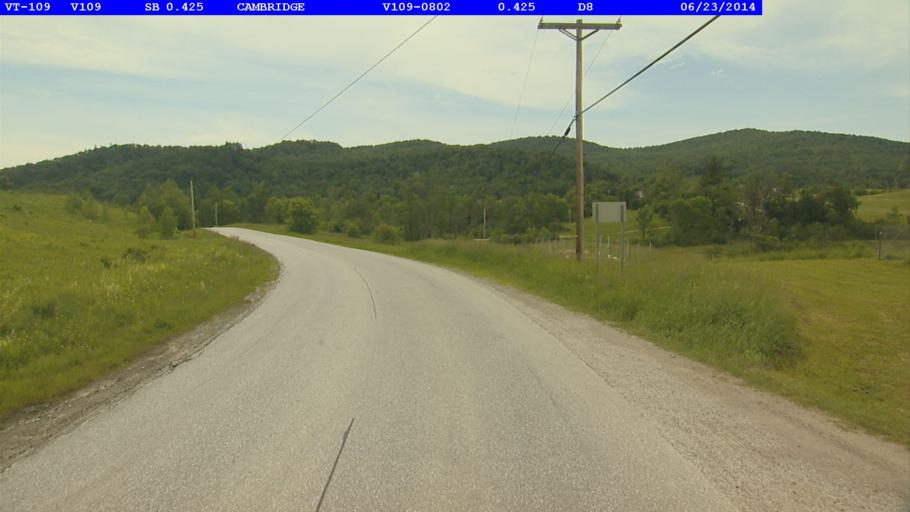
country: US
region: Vermont
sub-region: Lamoille County
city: Johnson
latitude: 44.6545
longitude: -72.8197
